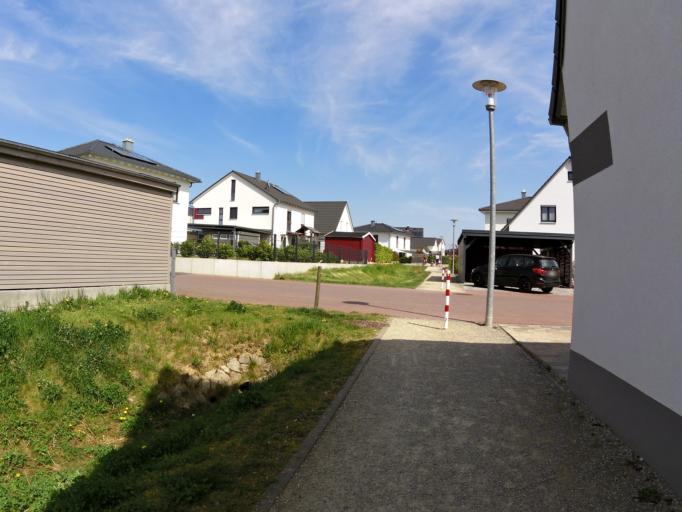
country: DE
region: Bavaria
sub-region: Regierungsbezirk Unterfranken
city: Unterpleichfeld
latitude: 49.8718
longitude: 10.0409
